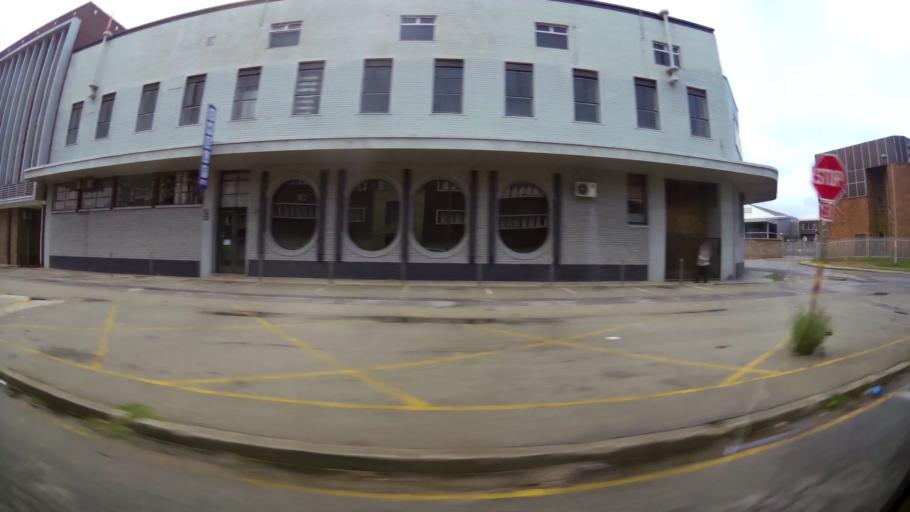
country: ZA
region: Eastern Cape
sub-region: Nelson Mandela Bay Metropolitan Municipality
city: Port Elizabeth
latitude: -33.9328
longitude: 25.6045
